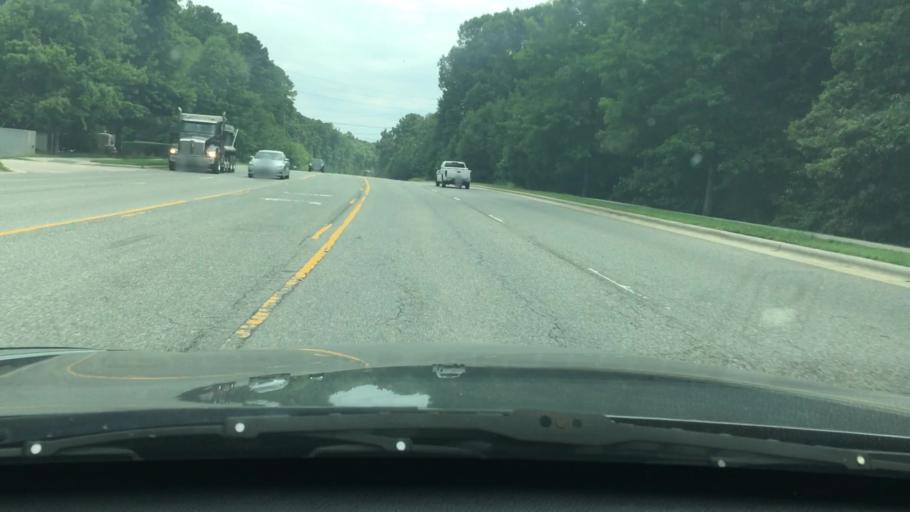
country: US
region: North Carolina
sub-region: Wake County
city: West Raleigh
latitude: 35.8510
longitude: -78.7112
